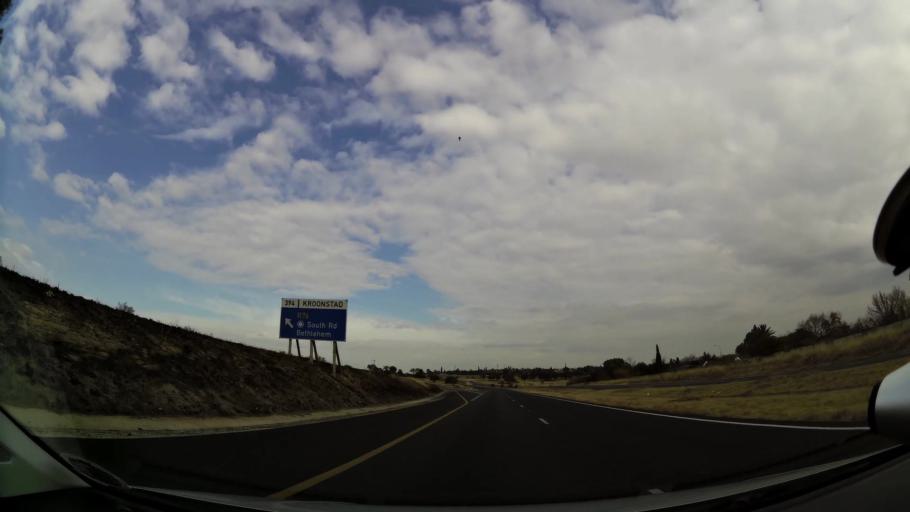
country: ZA
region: Orange Free State
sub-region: Fezile Dabi District Municipality
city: Kroonstad
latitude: -27.6830
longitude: 27.2456
